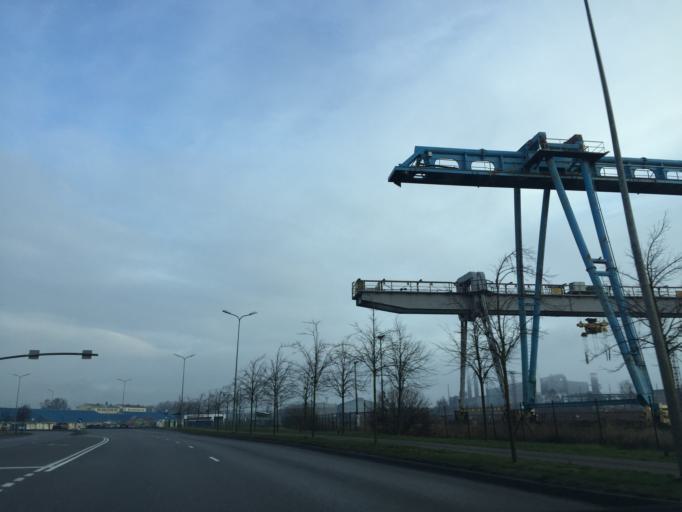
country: LV
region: Liepaja
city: Liepaja
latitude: 56.5198
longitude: 21.0273
